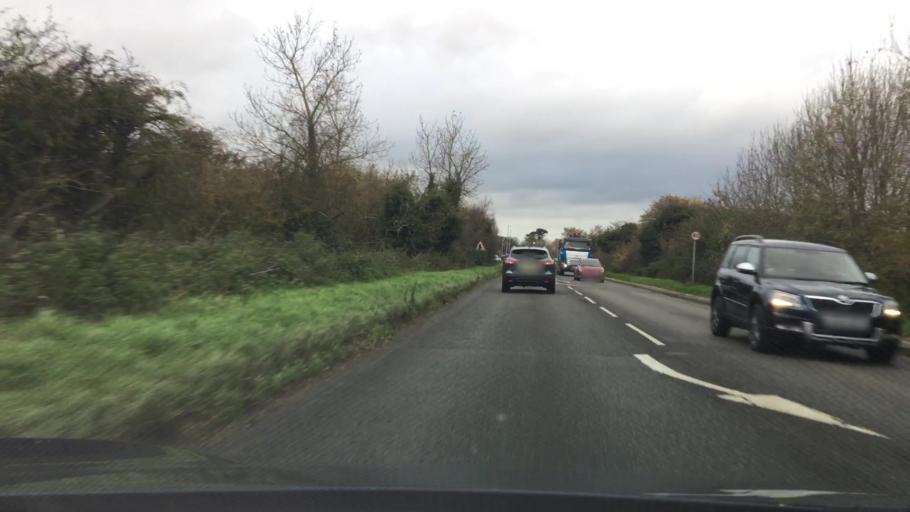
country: GB
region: England
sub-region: Nottinghamshire
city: Lowdham
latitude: 52.9913
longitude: -0.9903
